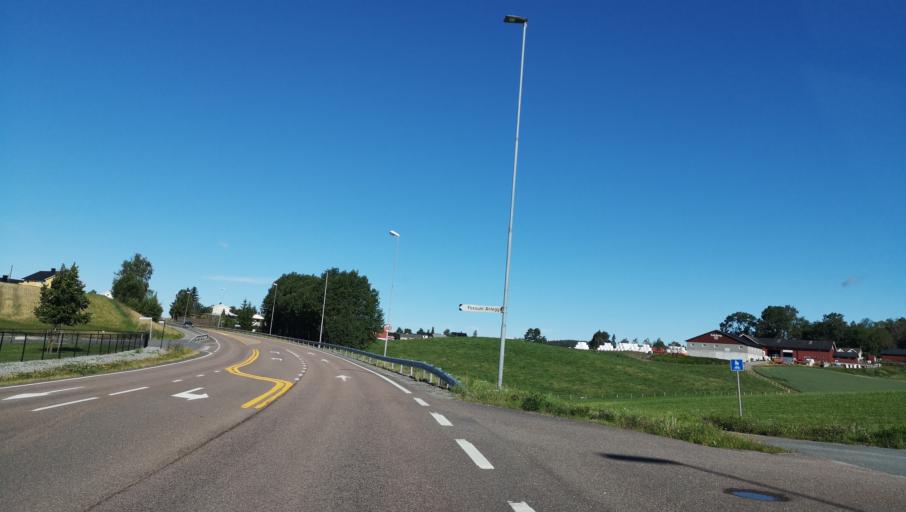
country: NO
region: Ostfold
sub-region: Spydeberg
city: Spydeberg
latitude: 59.6104
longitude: 11.0947
